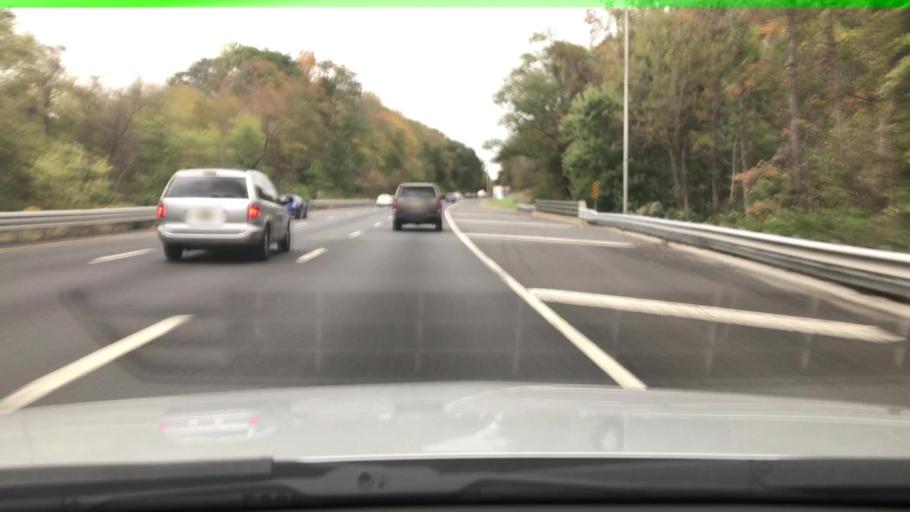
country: US
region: New Jersey
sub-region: Burlington County
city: Roebling
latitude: 40.0647
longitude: -74.7980
